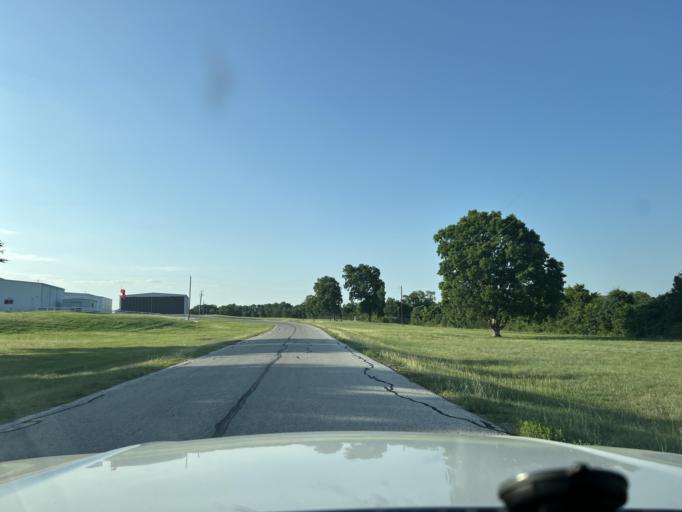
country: US
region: Texas
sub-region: Washington County
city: Brenham
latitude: 30.2195
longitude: -96.3717
